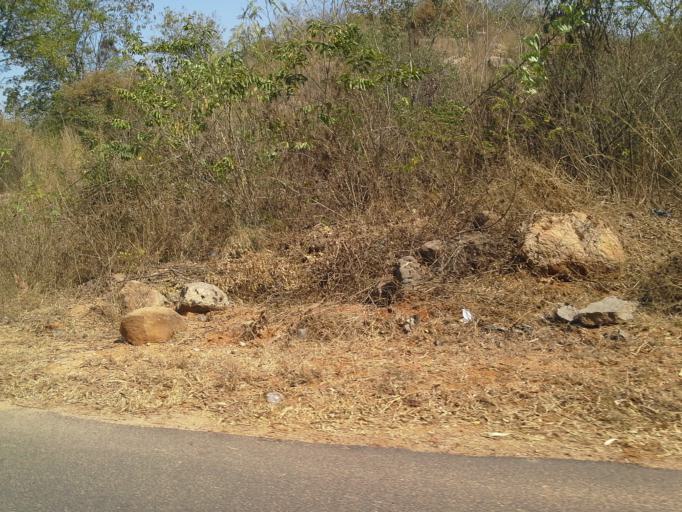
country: IN
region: Telangana
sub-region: Hyderabad
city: Hyderabad
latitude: 17.3111
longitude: 78.4146
